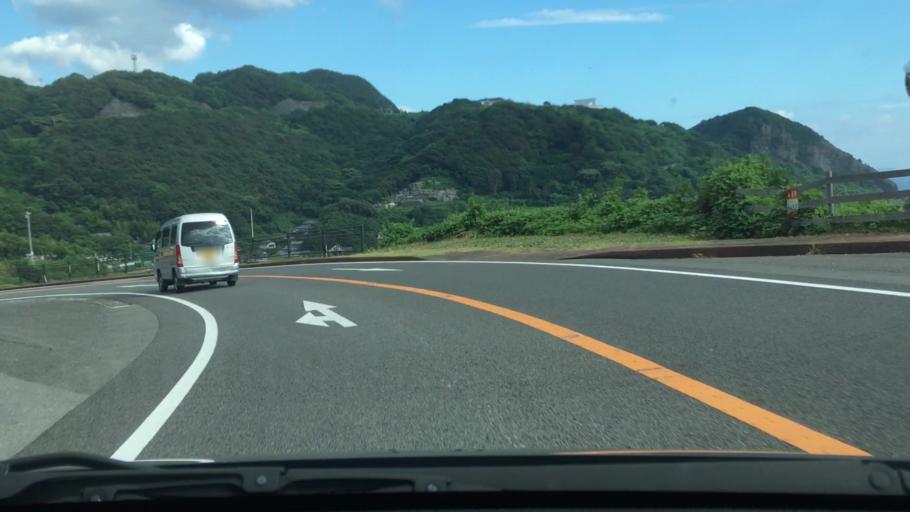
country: JP
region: Nagasaki
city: Togitsu
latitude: 32.8424
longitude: 129.6993
